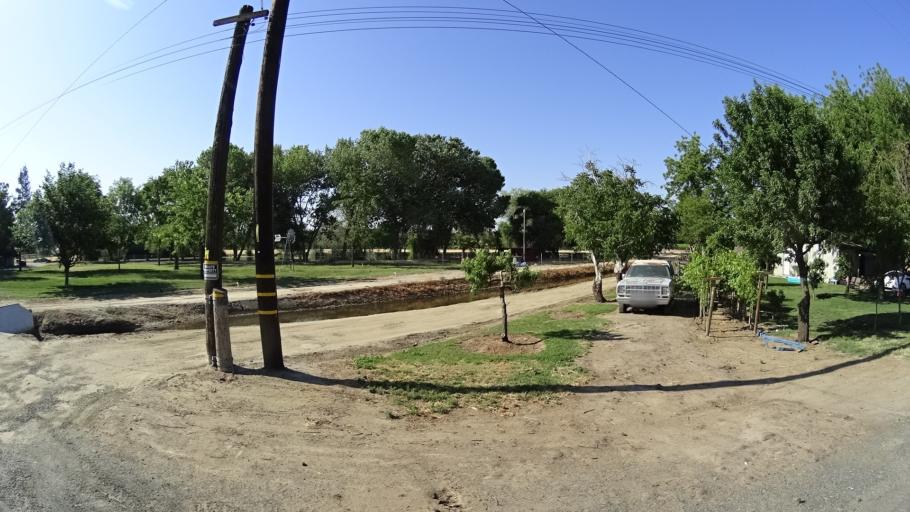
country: US
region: California
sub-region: Fresno County
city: Riverdale
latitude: 36.3658
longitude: -119.8378
